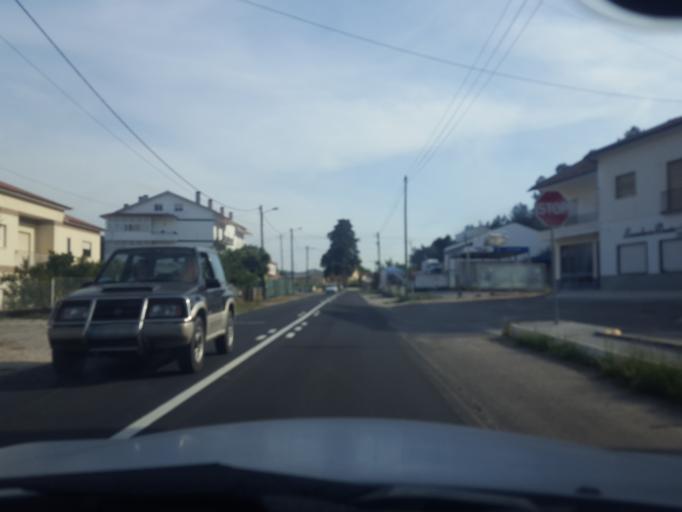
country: PT
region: Leiria
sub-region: Leiria
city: Leiria
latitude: 39.7147
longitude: -8.7889
